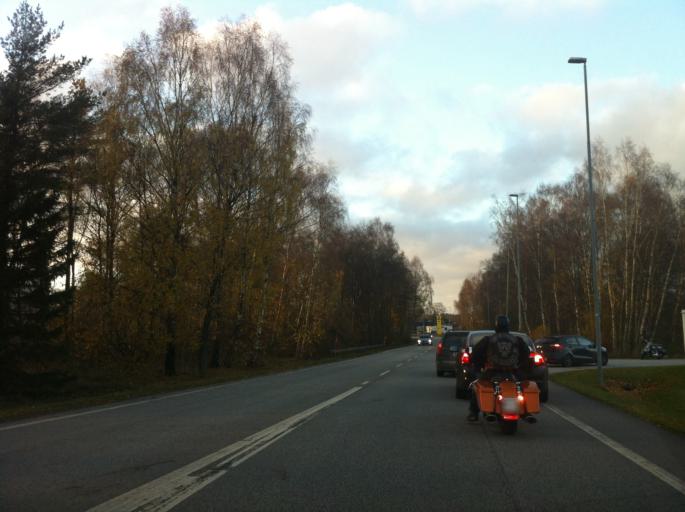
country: SE
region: Skane
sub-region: Hoors Kommun
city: Hoeoer
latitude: 55.9394
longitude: 13.5583
